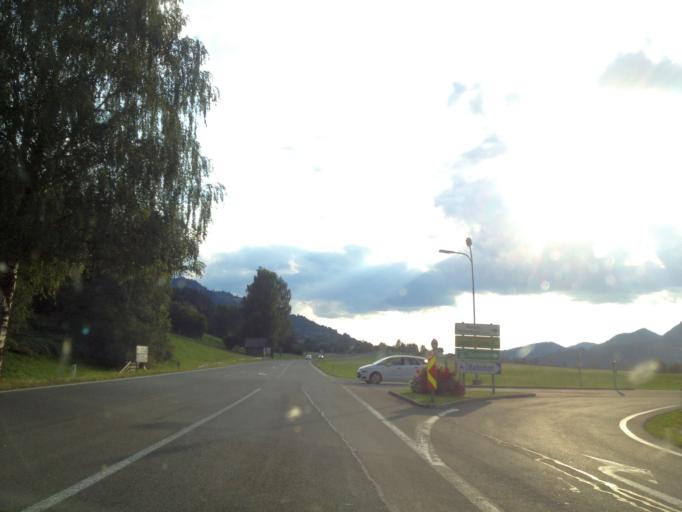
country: AT
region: Styria
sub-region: Politischer Bezirk Liezen
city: Aich
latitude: 47.4152
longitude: 13.8066
